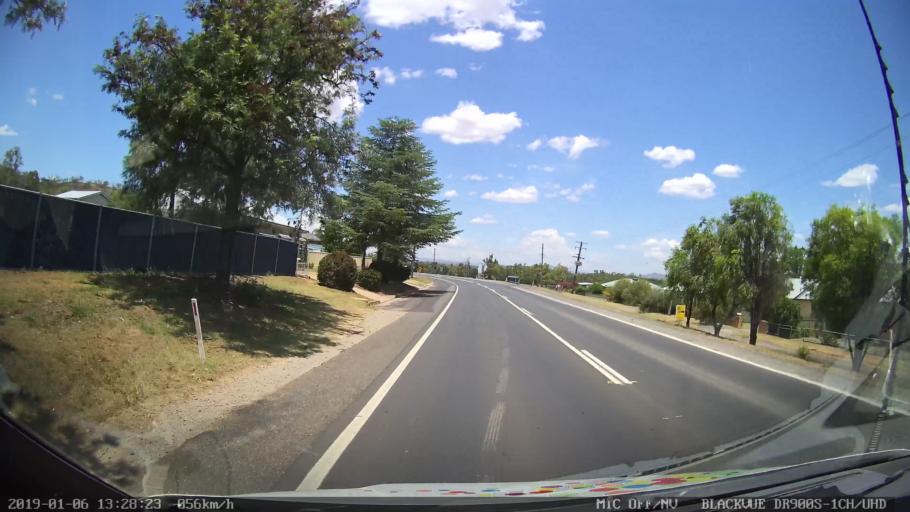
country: AU
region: New South Wales
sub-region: Tamworth Municipality
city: East Tamworth
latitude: -31.1157
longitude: 150.9624
